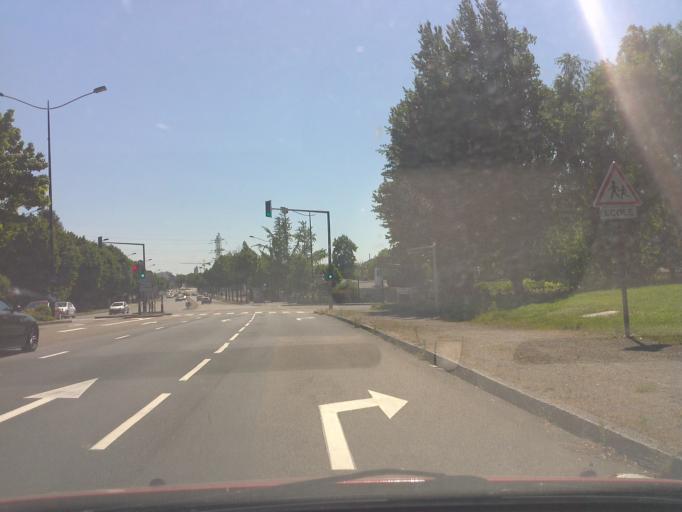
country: FR
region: Pays de la Loire
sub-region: Departement de la Loire-Atlantique
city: Sainte-Luce-sur-Loire
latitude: 47.2525
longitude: -1.5164
